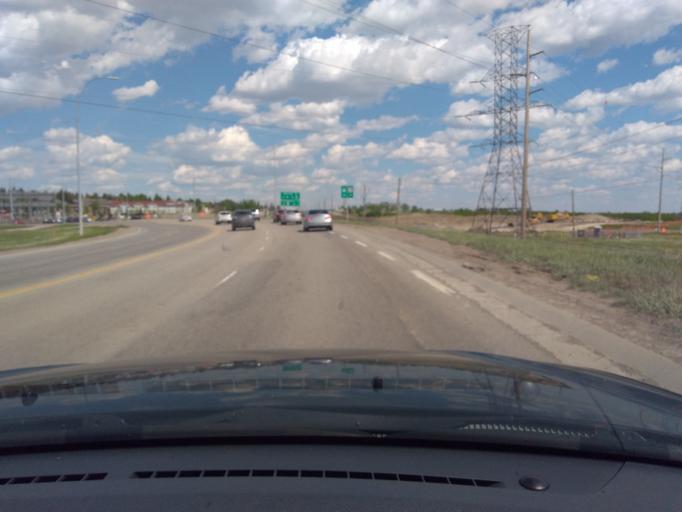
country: CA
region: Alberta
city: Calgary
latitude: 51.0088
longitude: -114.1664
